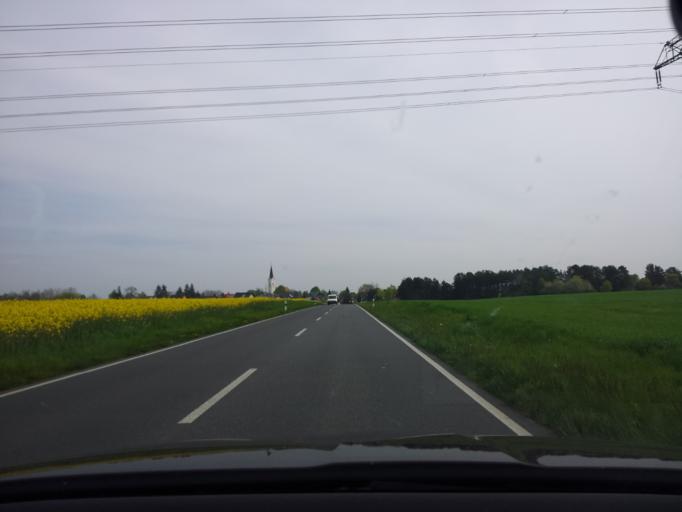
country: DE
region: Brandenburg
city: Lubbenau
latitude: 51.8573
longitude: 13.9243
